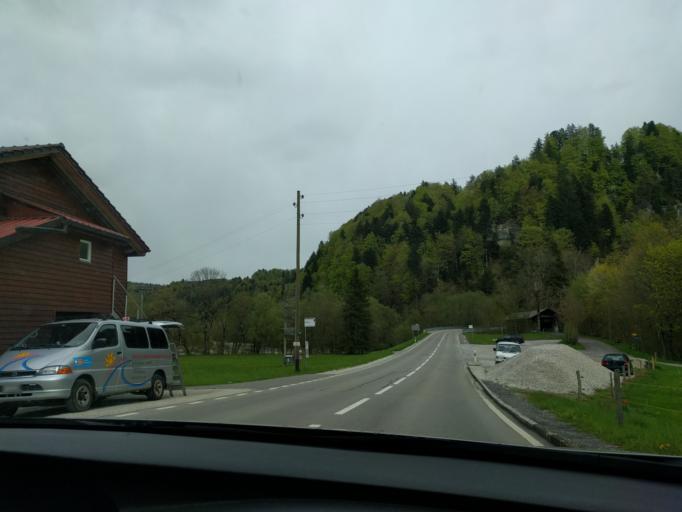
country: CH
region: Fribourg
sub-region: Sense District
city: Heitenried
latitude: 46.8255
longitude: 7.3177
